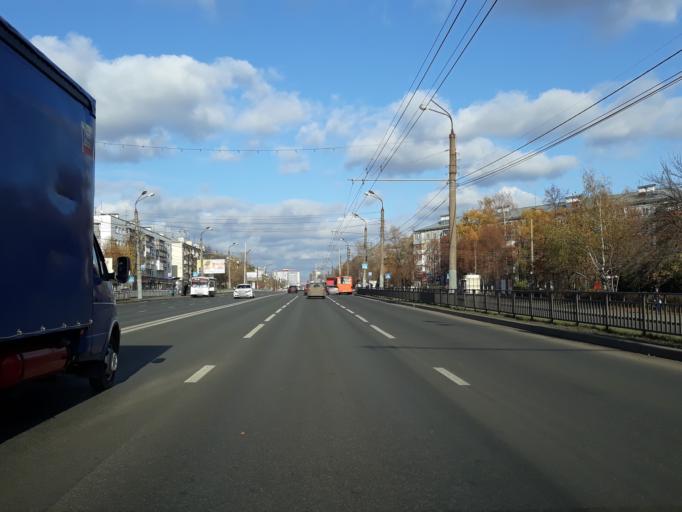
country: RU
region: Nizjnij Novgorod
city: Nizhniy Novgorod
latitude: 56.2887
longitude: 43.9307
